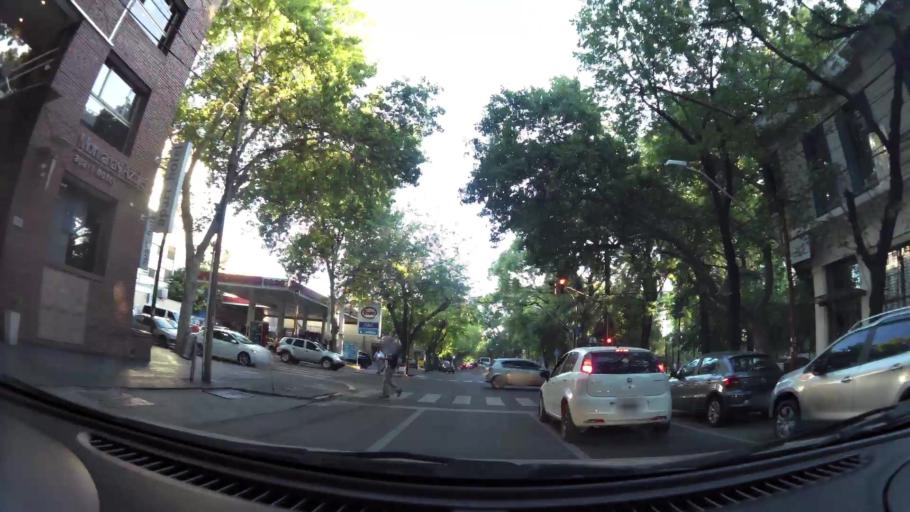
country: AR
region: Mendoza
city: Mendoza
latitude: -32.8870
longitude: -68.8478
